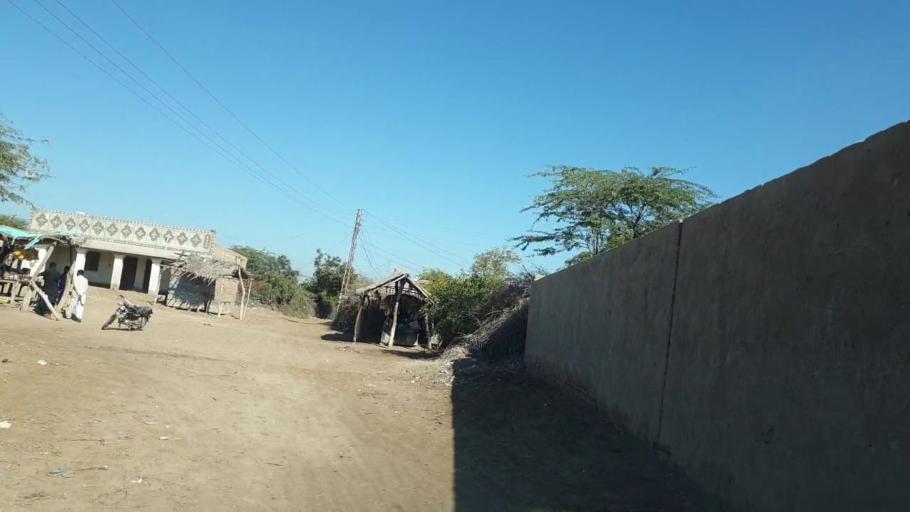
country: PK
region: Sindh
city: Jhol
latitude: 25.8075
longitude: 69.0324
